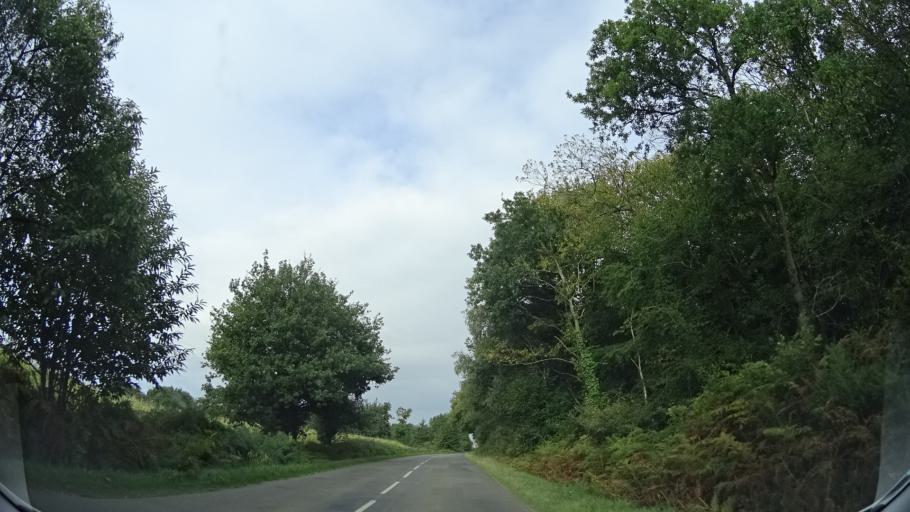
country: FR
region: Brittany
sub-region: Departement d'Ille-et-Vilaine
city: Guipel
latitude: 48.2997
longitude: -1.7559
